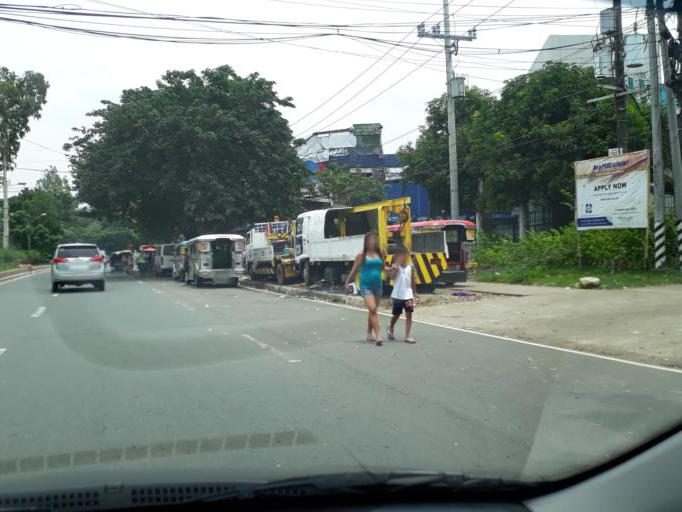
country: PH
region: Calabarzon
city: Bagong Pagasa
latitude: 14.6521
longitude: 121.0388
